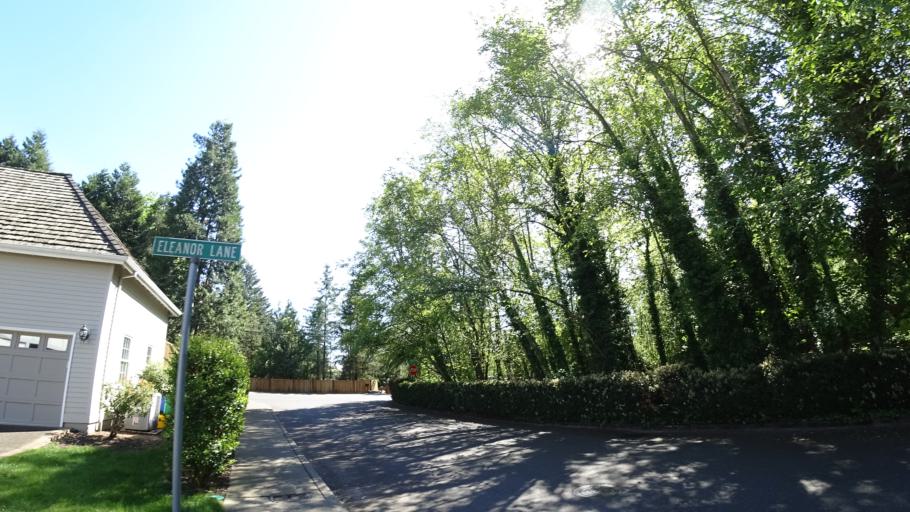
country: US
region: Oregon
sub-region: Washington County
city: Raleigh Hills
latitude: 45.4912
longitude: -122.7403
